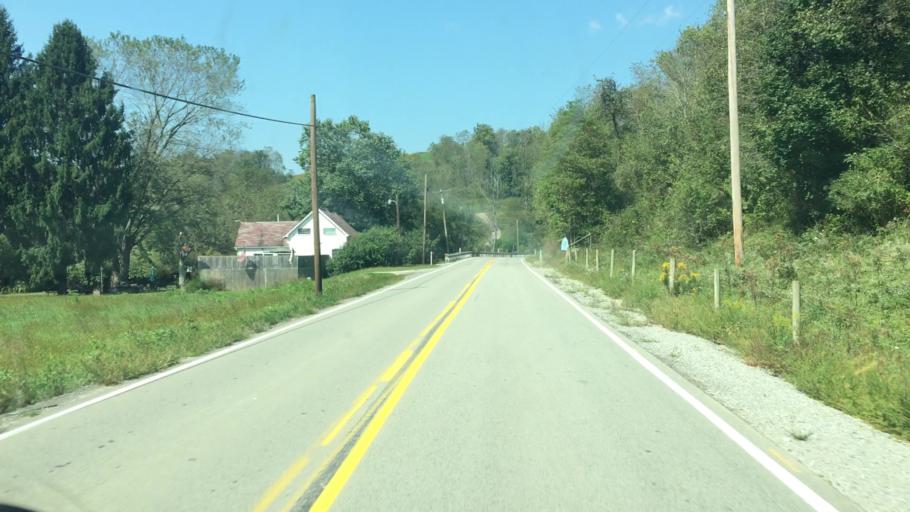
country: US
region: Pennsylvania
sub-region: Greene County
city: Waynesburg
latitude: 39.9538
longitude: -80.3046
